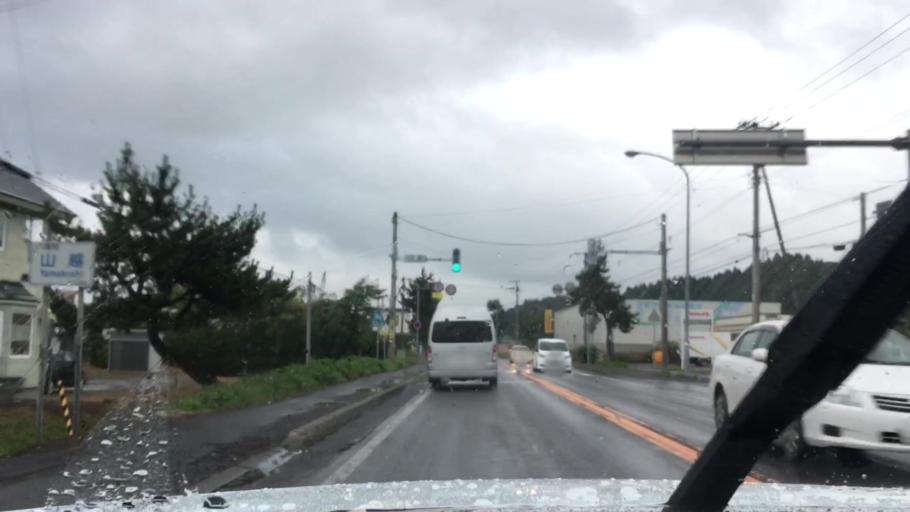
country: JP
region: Hokkaido
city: Nanae
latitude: 42.2324
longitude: 140.3250
